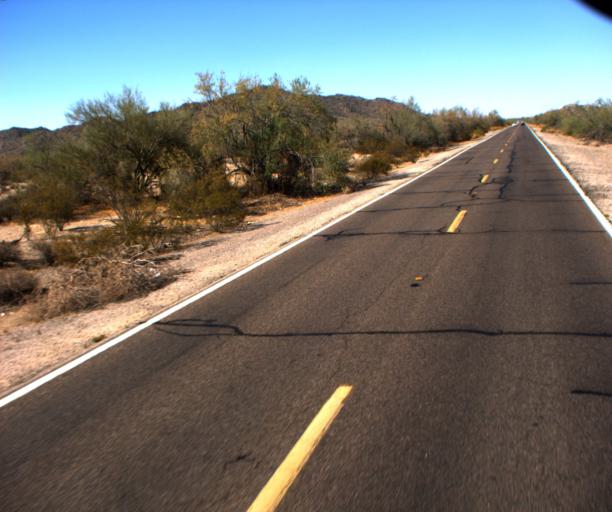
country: US
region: Arizona
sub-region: Pinal County
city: Sacaton
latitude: 33.0235
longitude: -111.7400
